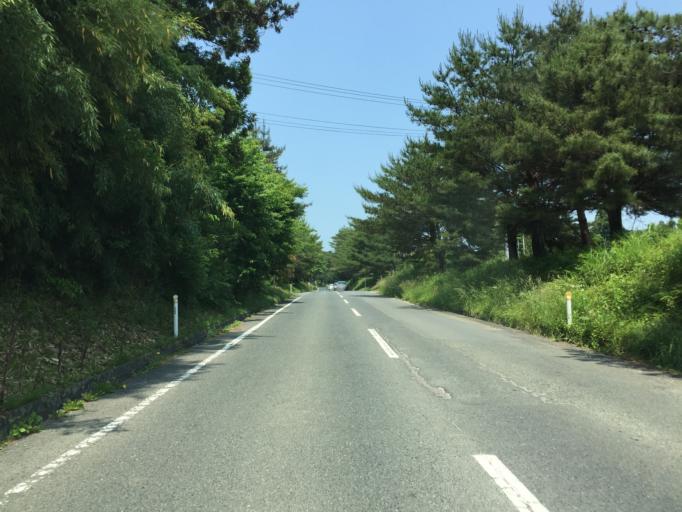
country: JP
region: Miyagi
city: Marumori
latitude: 37.7698
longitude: 140.9382
